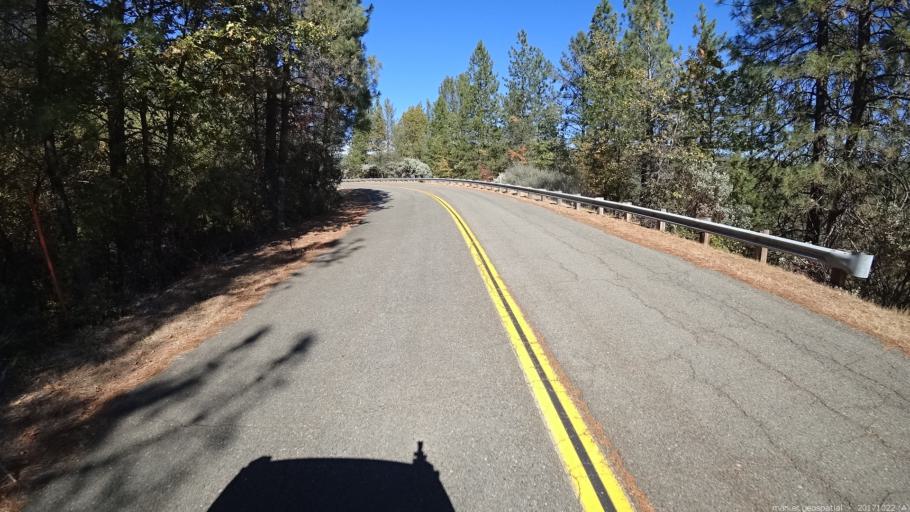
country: US
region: California
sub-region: Shasta County
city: Central Valley (historical)
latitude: 40.9202
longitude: -122.4024
